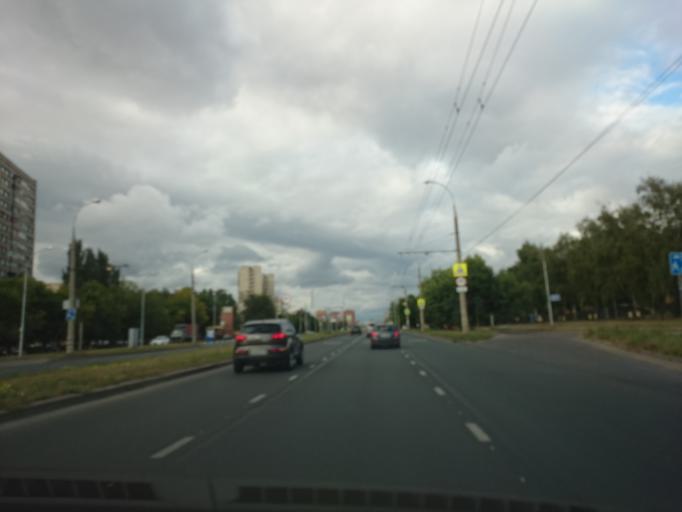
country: RU
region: Samara
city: Tol'yatti
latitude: 53.5053
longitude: 49.3005
